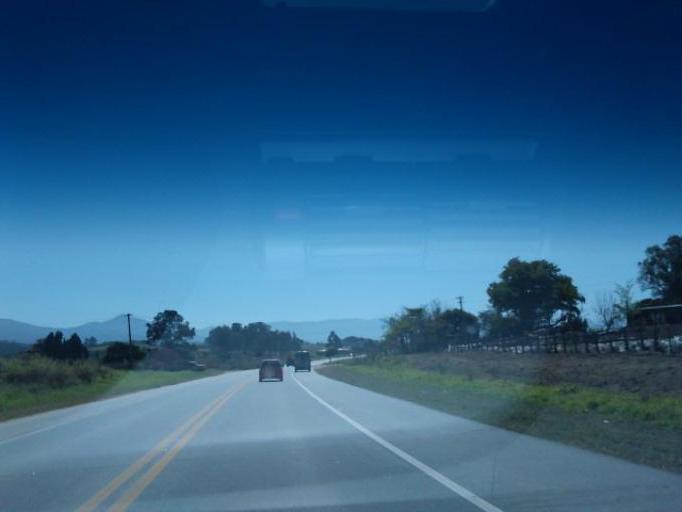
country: BR
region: Sao Paulo
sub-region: Tremembe
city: Tremembe
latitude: -22.9819
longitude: -45.6490
